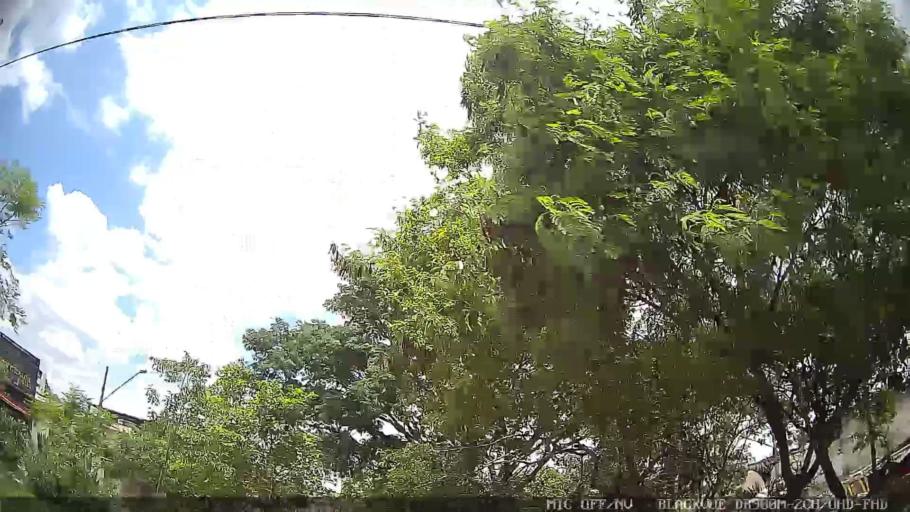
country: BR
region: Sao Paulo
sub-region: Guarulhos
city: Guarulhos
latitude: -23.5149
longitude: -46.5478
